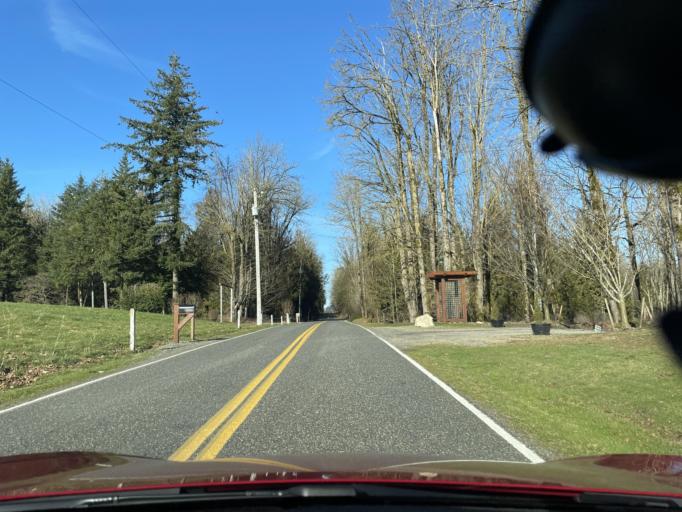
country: US
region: Washington
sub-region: Whatcom County
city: Lynden
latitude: 48.9873
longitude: -122.5295
